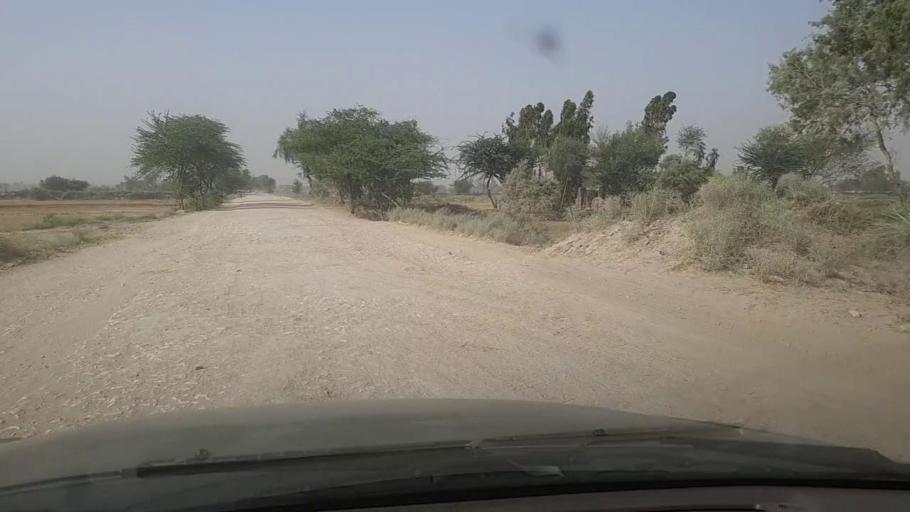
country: PK
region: Sindh
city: Shikarpur
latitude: 27.9287
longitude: 68.6164
